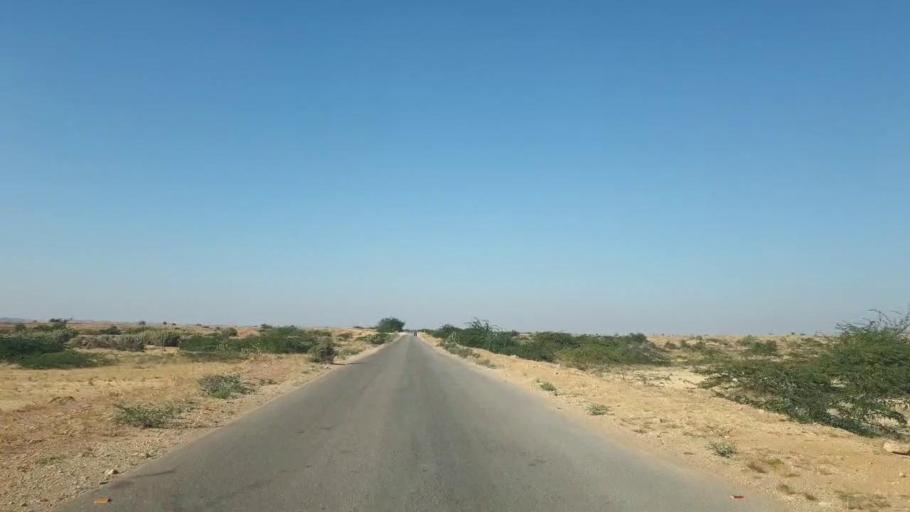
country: PK
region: Sindh
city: Malir Cantonment
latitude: 25.2550
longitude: 67.6021
